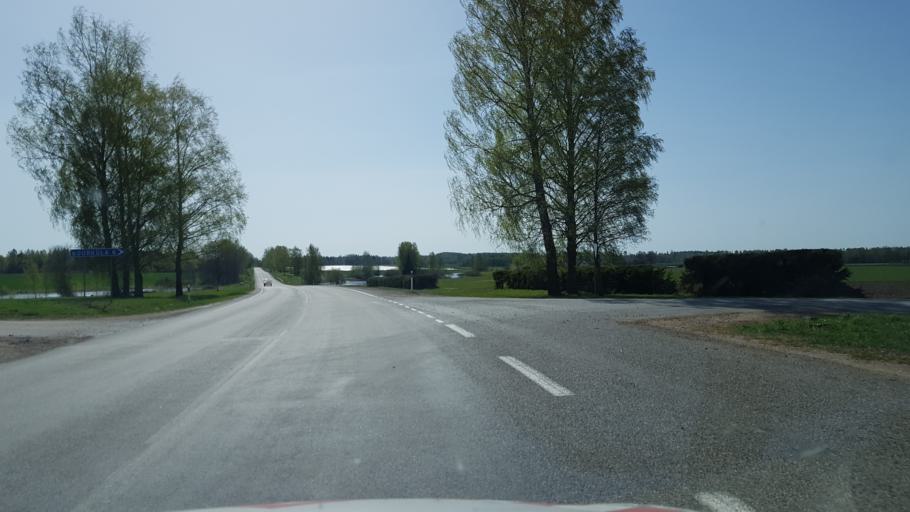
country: EE
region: Valgamaa
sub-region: Torva linn
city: Torva
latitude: 57.9547
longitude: 25.9696
